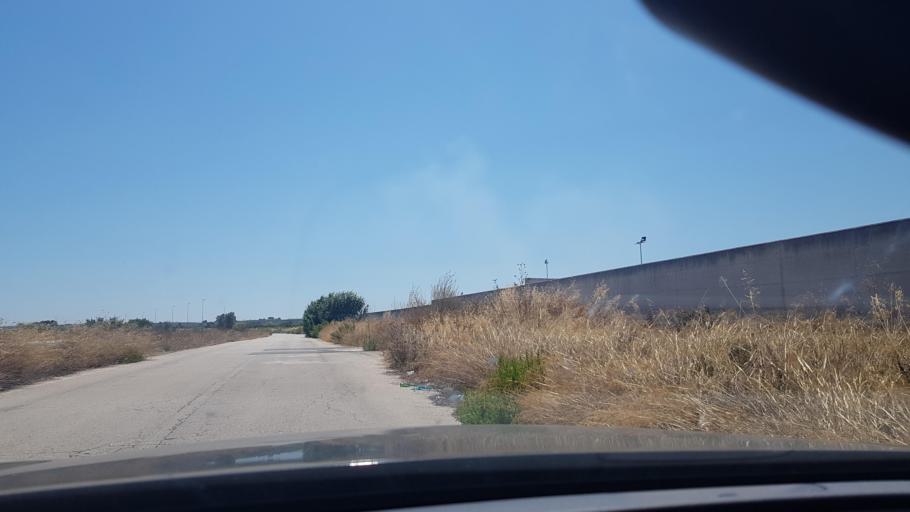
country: IT
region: Apulia
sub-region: Provincia di Barletta - Andria - Trani
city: Barletta
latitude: 41.3070
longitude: 16.3283
